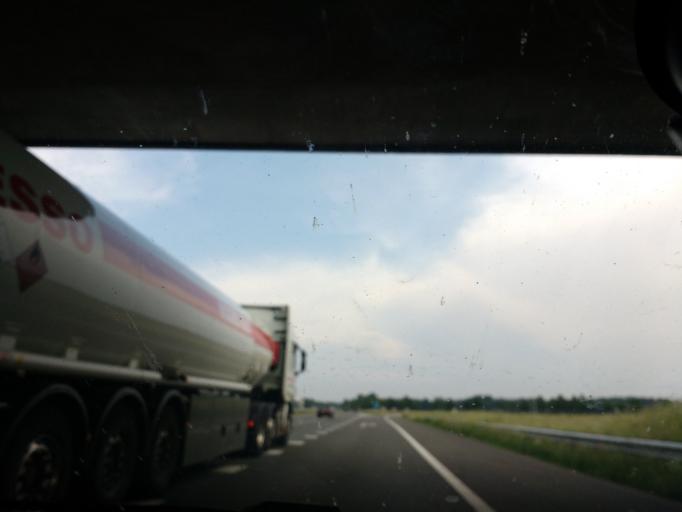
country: NL
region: North Brabant
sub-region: Gemeente Boxmeer
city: Overloon
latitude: 51.5853
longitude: 5.9795
